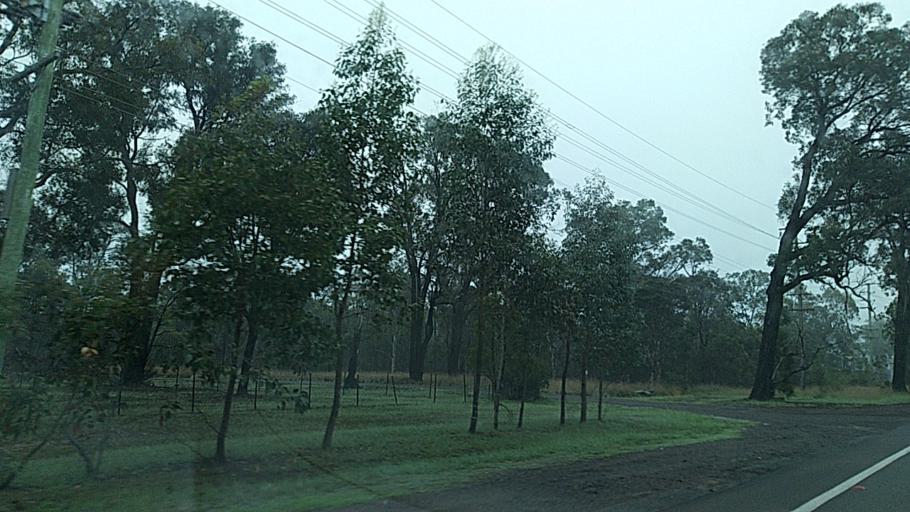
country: AU
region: New South Wales
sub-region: Penrith Municipality
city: Werrington Downs
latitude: -33.6810
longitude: 150.7412
